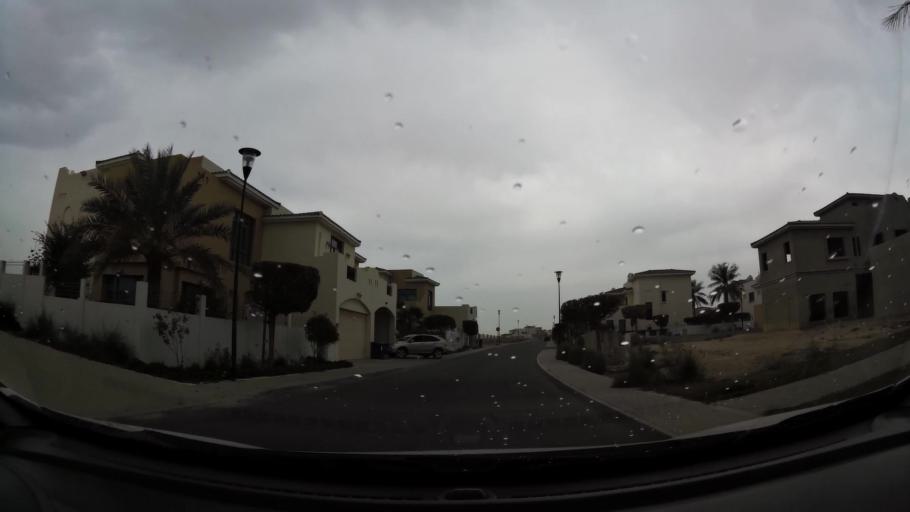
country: BH
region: Northern
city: Ar Rifa'
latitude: 26.0875
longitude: 50.5580
